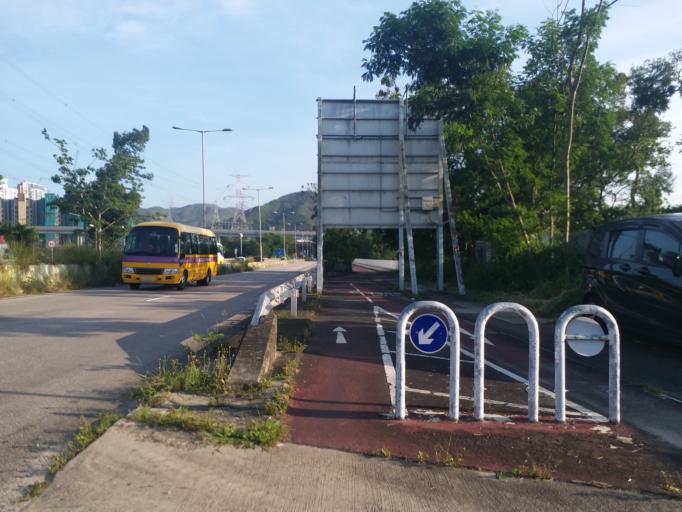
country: HK
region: Yuen Long
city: Yuen Long Kau Hui
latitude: 22.4505
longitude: 114.0502
